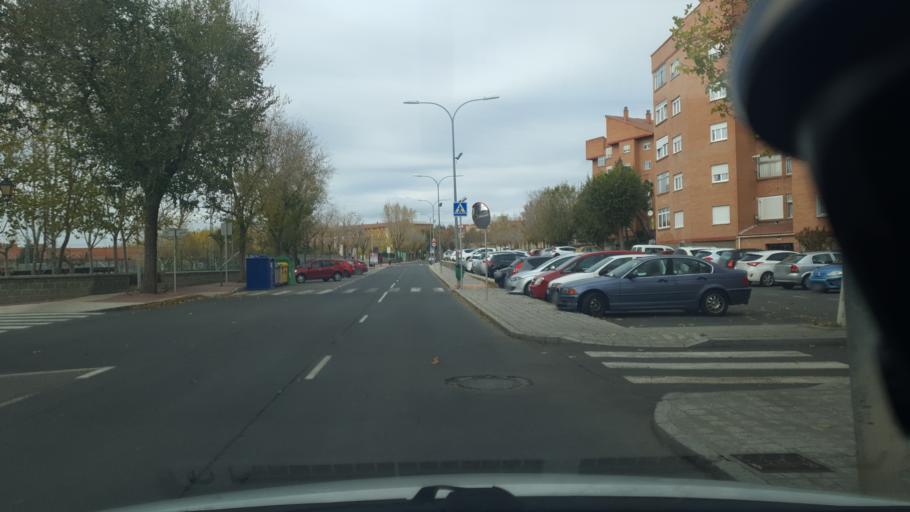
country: ES
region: Castille and Leon
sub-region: Provincia de Avila
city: Avila
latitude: 40.6470
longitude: -4.6849
